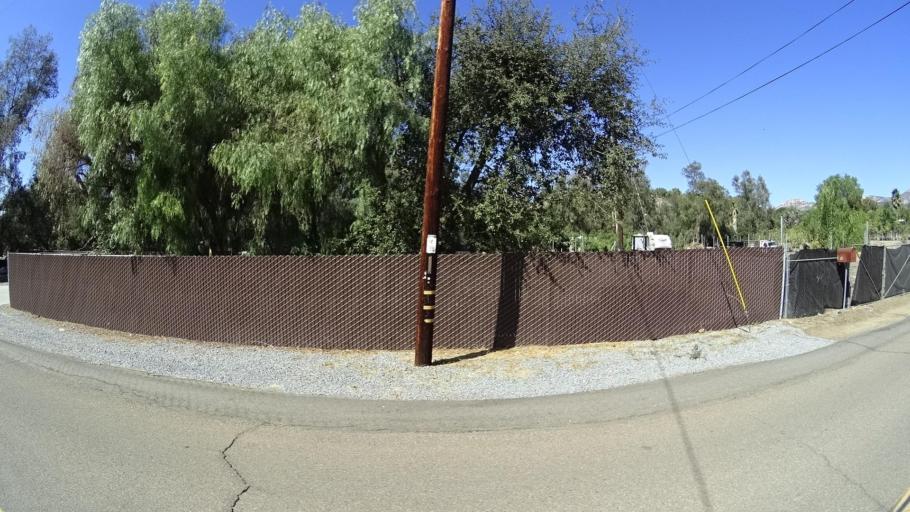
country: US
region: California
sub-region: San Diego County
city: Harbison Canyon
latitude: 32.8600
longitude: -116.8568
